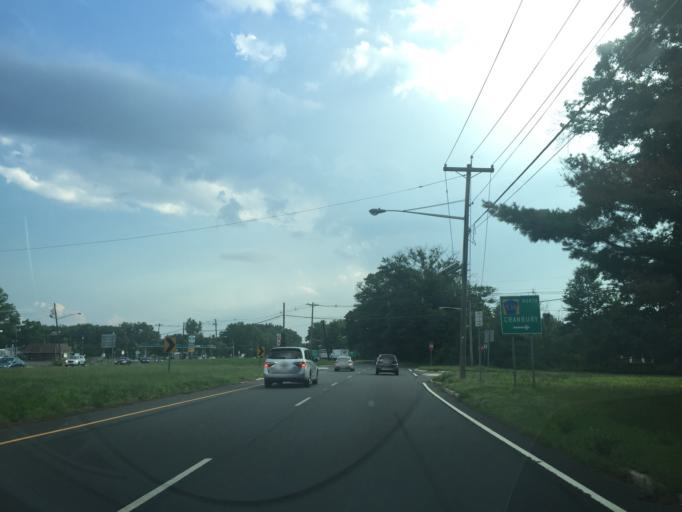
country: US
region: New Jersey
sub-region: Mercer County
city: Hightstown
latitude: 40.2930
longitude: -74.5197
